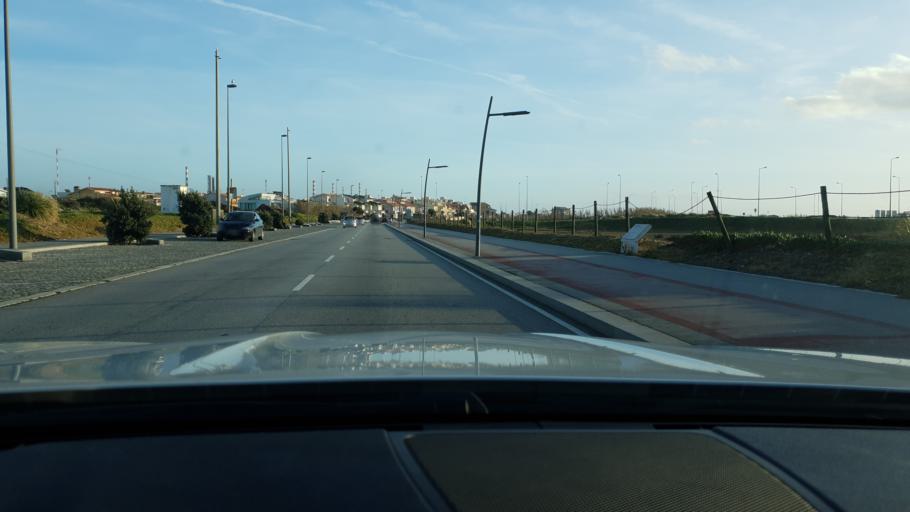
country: PT
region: Porto
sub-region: Matosinhos
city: Lavra
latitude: 41.2324
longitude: -8.7201
